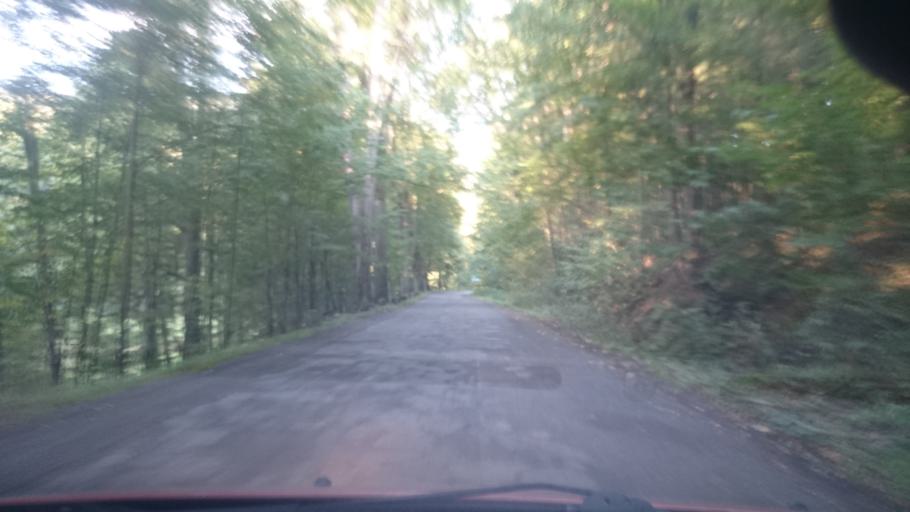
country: PL
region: Lower Silesian Voivodeship
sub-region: Powiat klodzki
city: Bystrzyca Klodzka
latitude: 50.3012
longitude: 16.5569
